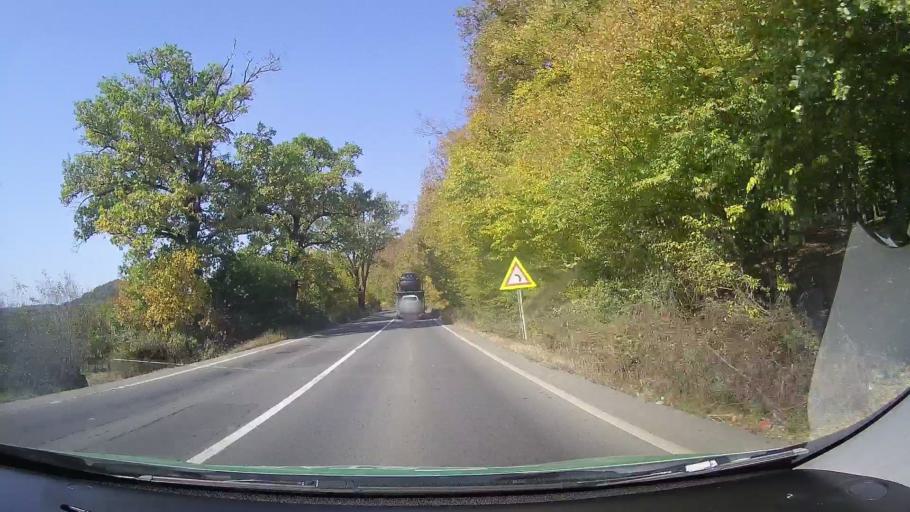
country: RO
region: Arad
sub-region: Comuna Conop
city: Conop
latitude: 46.1115
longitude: 21.8482
